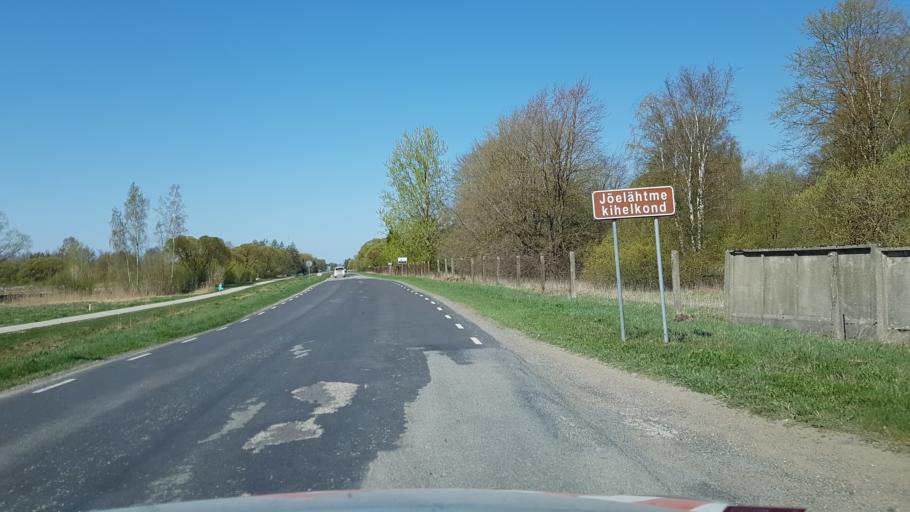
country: EE
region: Harju
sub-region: Joelaehtme vald
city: Loo
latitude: 59.4280
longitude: 24.9442
